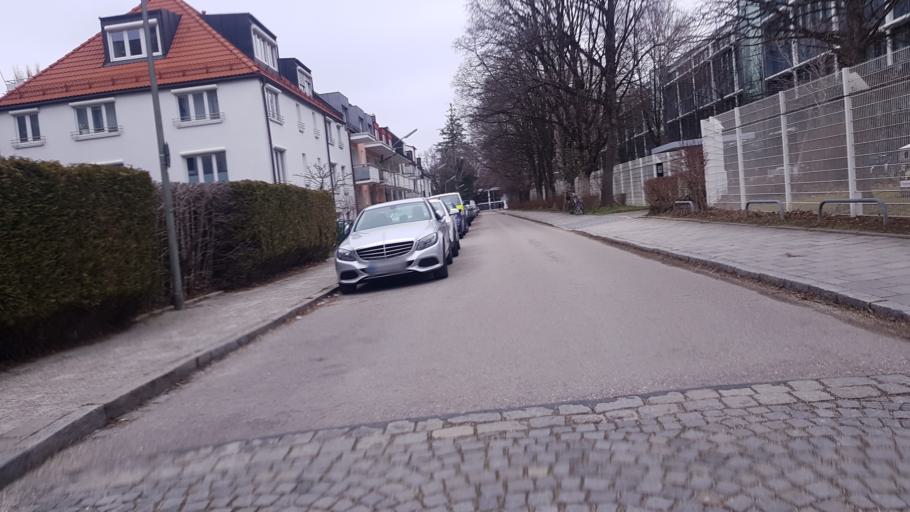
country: DE
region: Bavaria
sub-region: Upper Bavaria
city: Bogenhausen
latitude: 48.1394
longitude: 11.6215
